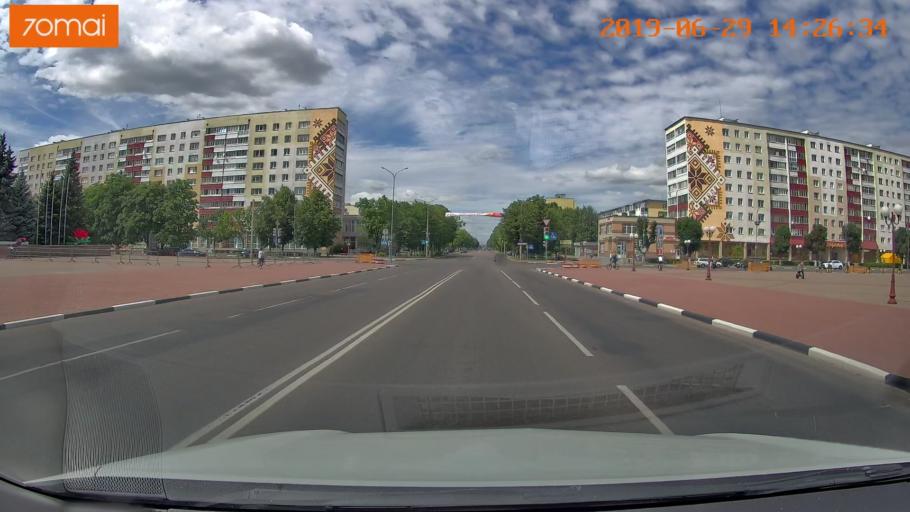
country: BY
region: Minsk
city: Salihorsk
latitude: 52.7836
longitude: 27.5411
